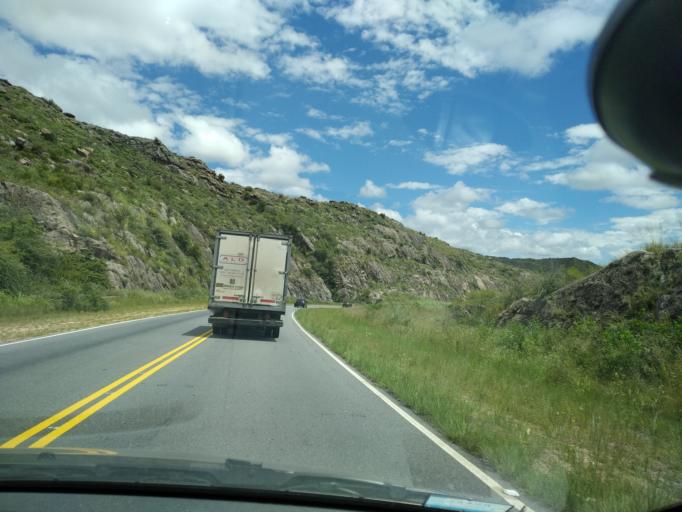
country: AR
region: Cordoba
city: Cuesta Blanca
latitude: -31.6154
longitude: -64.6719
